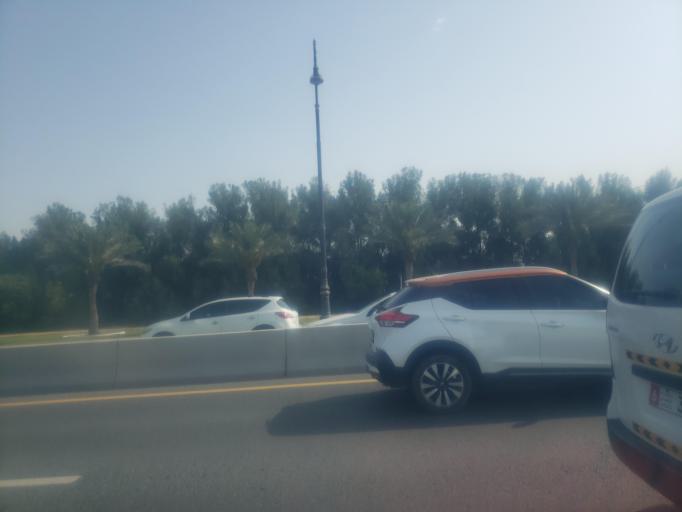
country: AE
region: Ash Shariqah
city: Sharjah
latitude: 25.3288
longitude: 55.4784
